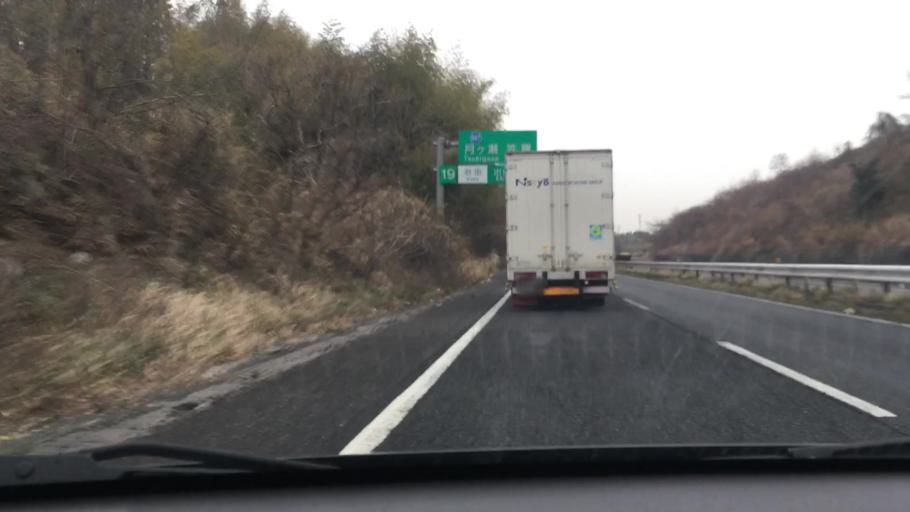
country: JP
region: Mie
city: Nabari
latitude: 34.6996
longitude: 136.0636
